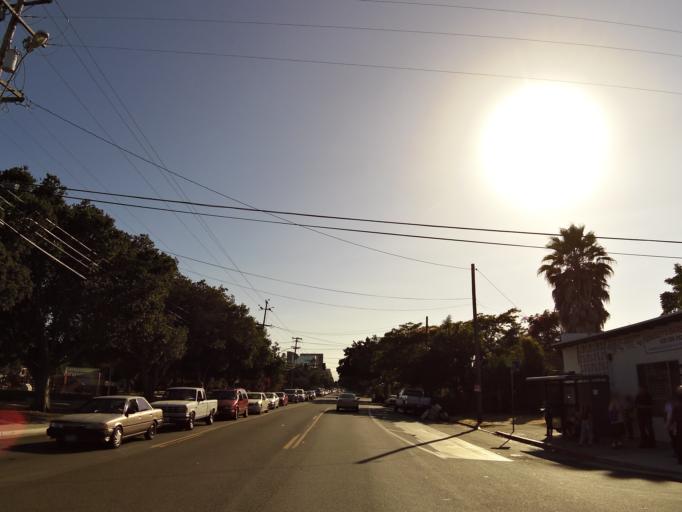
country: US
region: California
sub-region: Santa Clara County
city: San Jose
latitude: 37.3569
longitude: -121.8960
